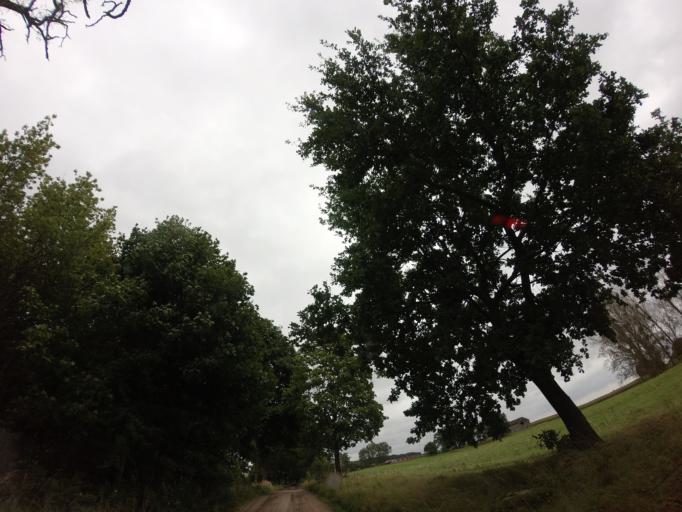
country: PL
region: West Pomeranian Voivodeship
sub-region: Powiat choszczenski
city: Choszczno
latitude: 53.1635
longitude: 15.3664
